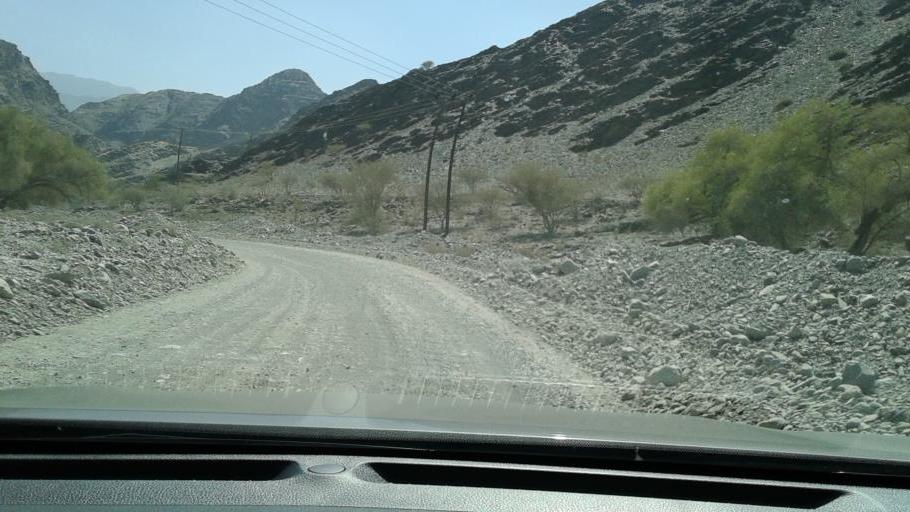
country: OM
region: Al Batinah
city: Bayt al `Awabi
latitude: 23.2618
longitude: 57.4422
